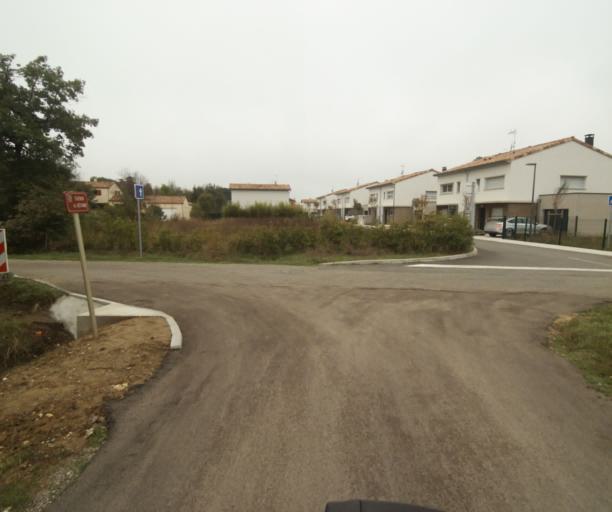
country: FR
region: Midi-Pyrenees
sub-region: Departement du Tarn-et-Garonne
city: Orgueil
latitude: 43.9048
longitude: 1.4146
